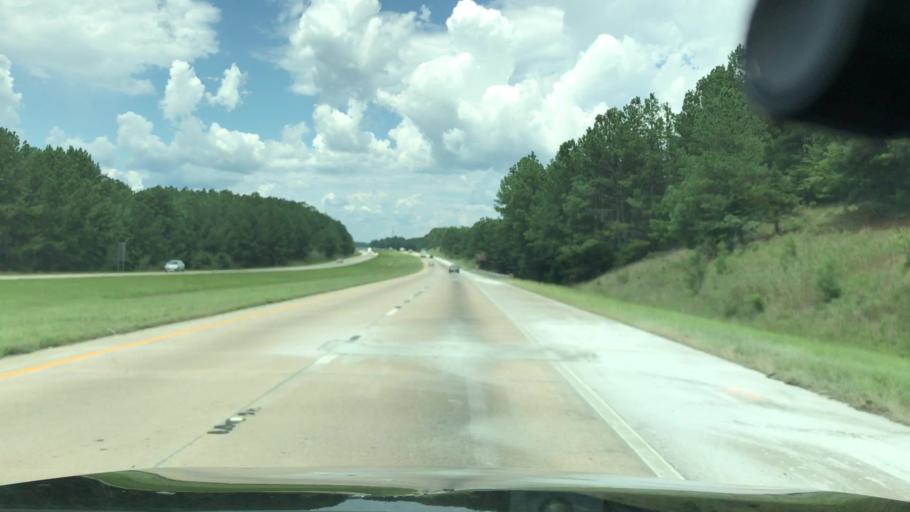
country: US
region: South Carolina
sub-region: Fairfield County
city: Winnsboro
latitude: 34.3928
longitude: -80.9937
